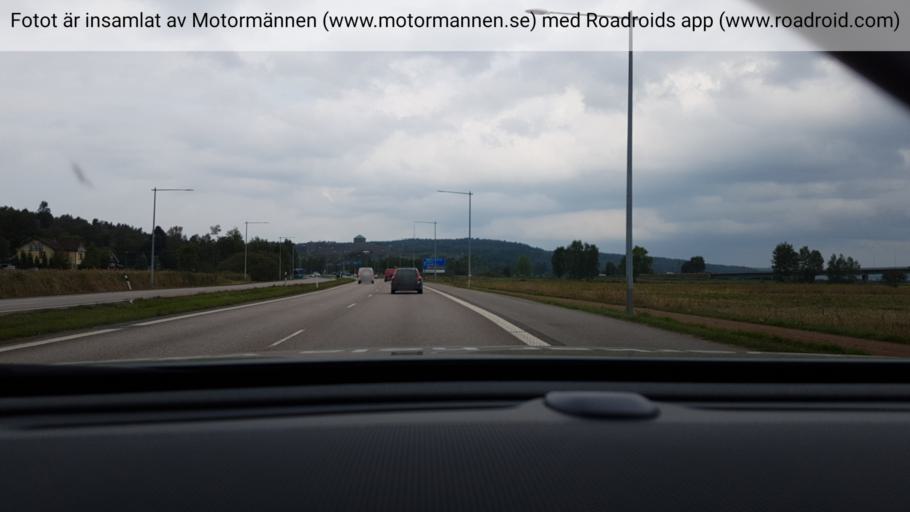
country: SE
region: Vaestra Goetaland
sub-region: Kungalvs Kommun
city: Kungalv
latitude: 57.8521
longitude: 12.0020
